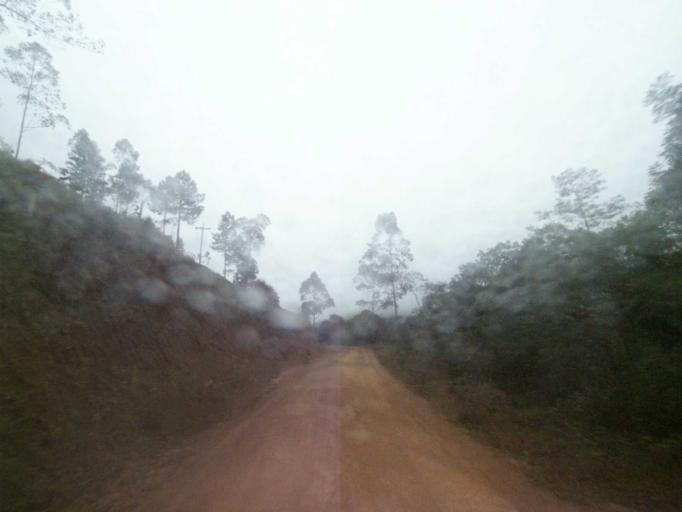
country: BR
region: Santa Catarina
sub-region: Anitapolis
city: Anitapolis
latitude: -27.8855
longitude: -49.1327
